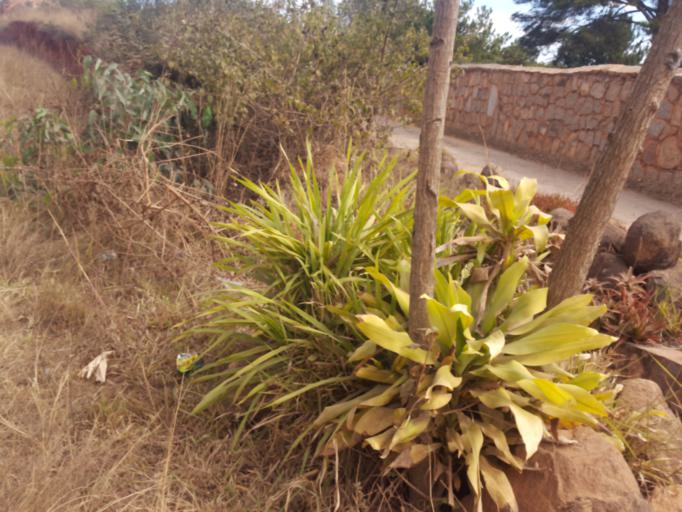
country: MG
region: Analamanga
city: Antananarivo
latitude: -18.9518
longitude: 47.3605
